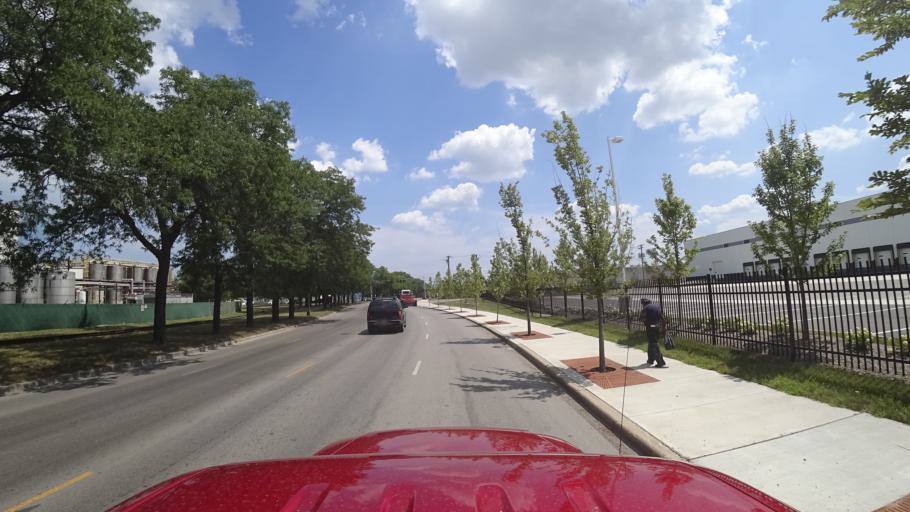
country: US
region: Illinois
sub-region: Cook County
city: Chicago
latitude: 41.8157
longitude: -87.6616
